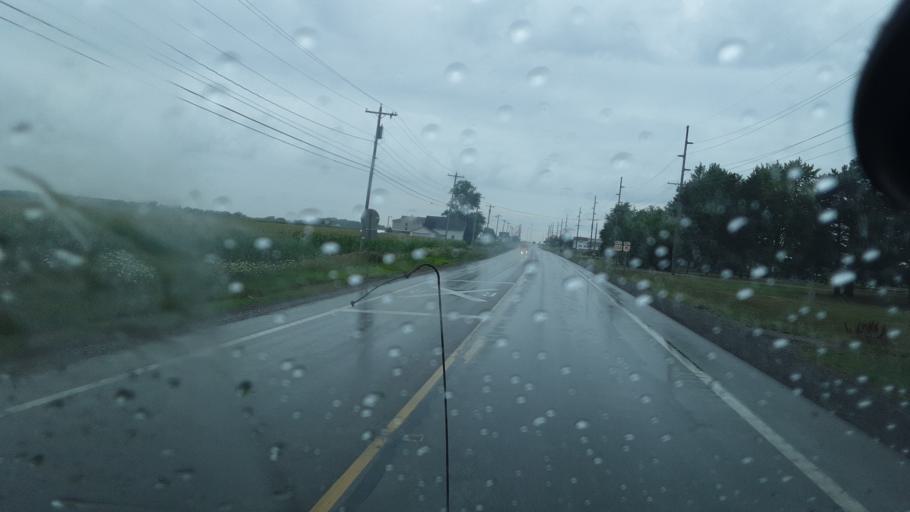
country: US
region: Ohio
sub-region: Williams County
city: Montpelier
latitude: 41.6020
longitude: -84.5557
